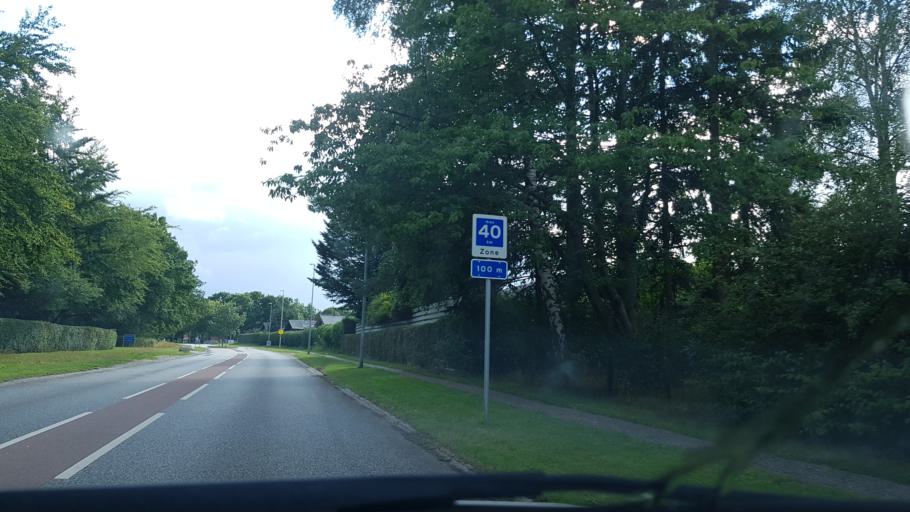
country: DK
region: Capital Region
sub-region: Fredensborg Kommune
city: Kokkedal
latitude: 55.9120
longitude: 12.4910
